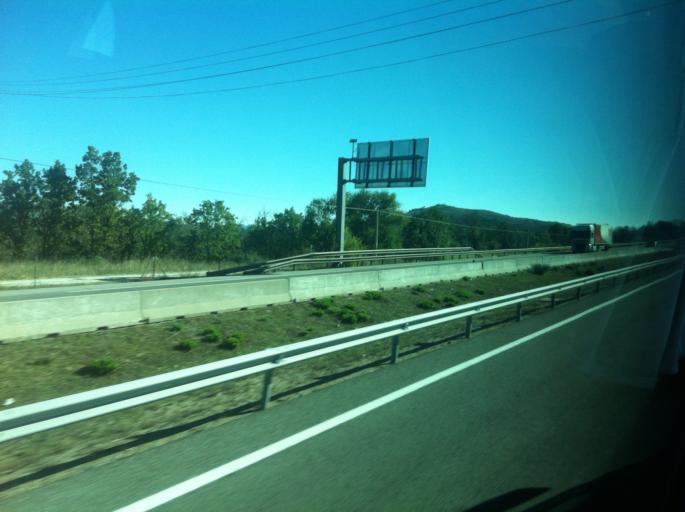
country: ES
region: Madrid
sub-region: Provincia de Madrid
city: Braojos
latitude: 41.0468
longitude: -3.6159
